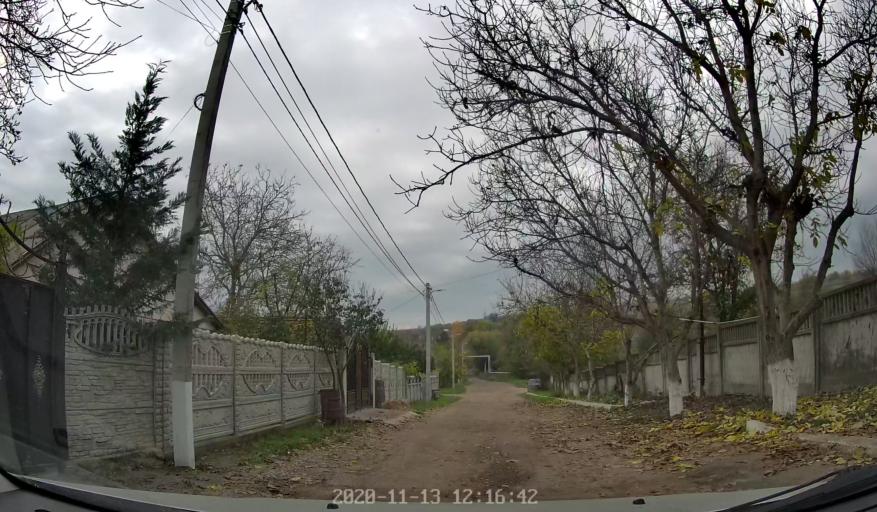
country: MD
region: Laloveni
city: Ialoveni
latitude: 46.9493
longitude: 28.8372
